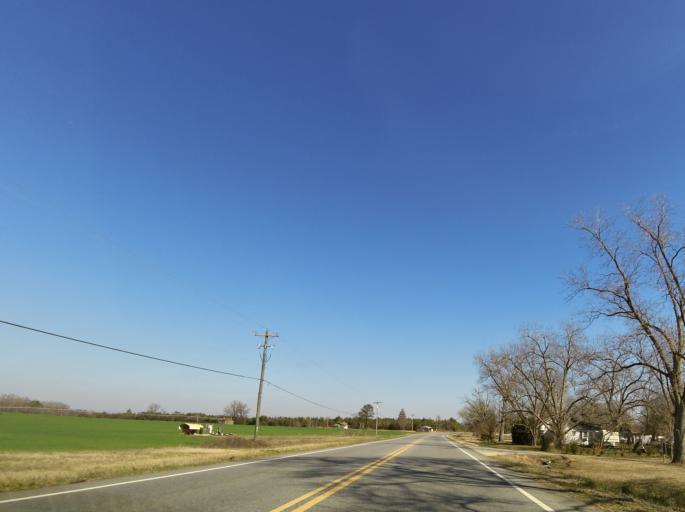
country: US
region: Georgia
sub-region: Bleckley County
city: Cochran
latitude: 32.3456
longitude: -83.3977
